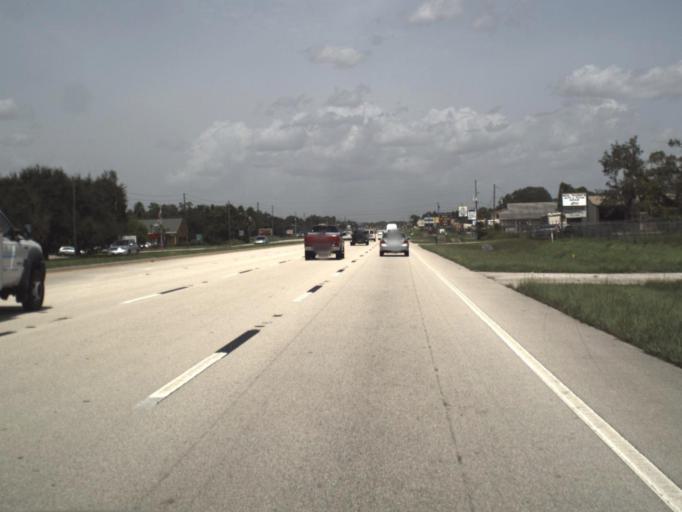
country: US
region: Florida
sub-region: Highlands County
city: Sebring
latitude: 27.4343
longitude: -81.4184
